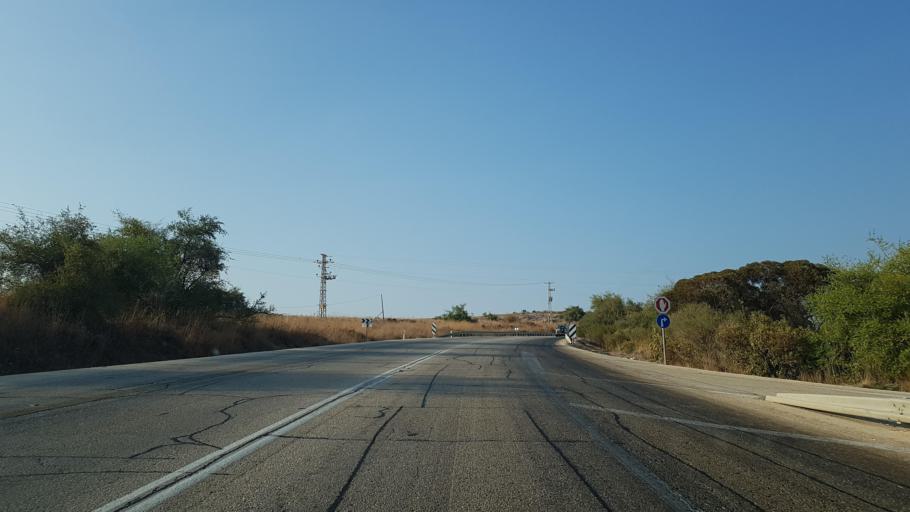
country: SY
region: Quneitra
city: Al Butayhah
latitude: 32.9059
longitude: 35.5973
